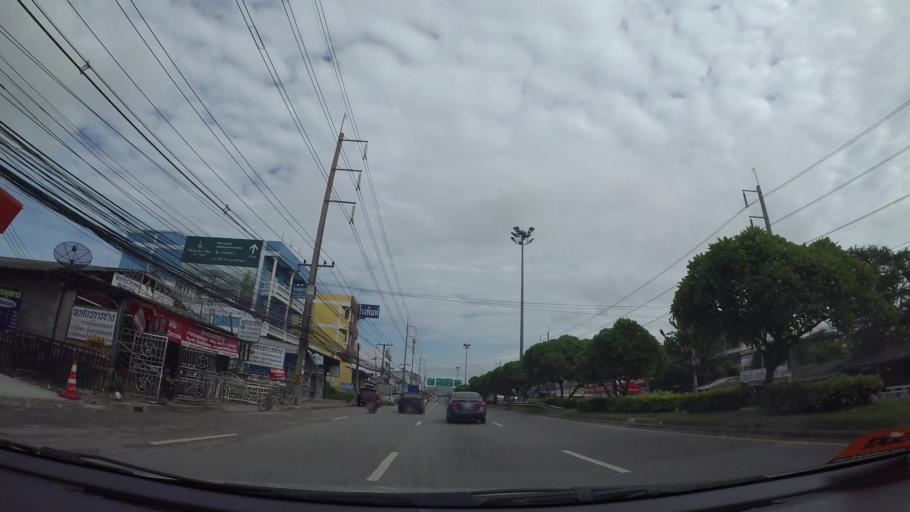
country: TH
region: Rayong
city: Rayong
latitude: 12.7117
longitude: 101.1709
